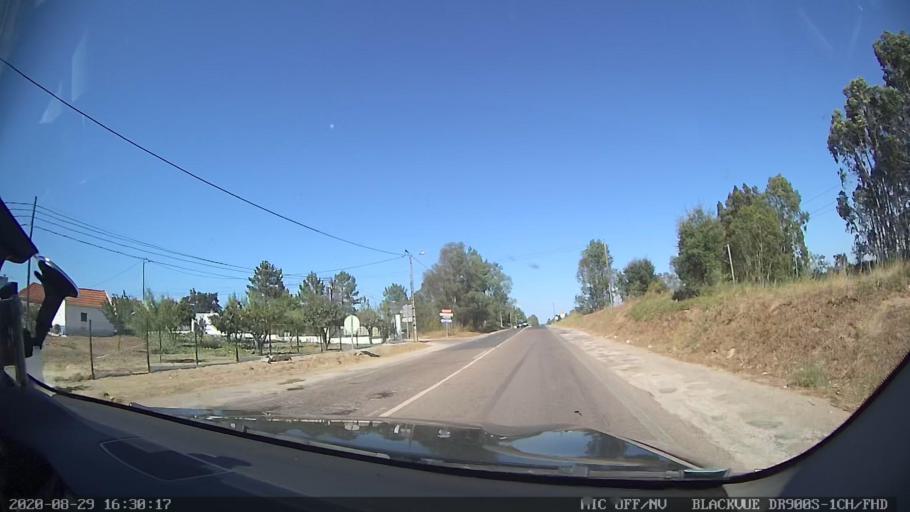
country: PT
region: Setubal
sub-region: Setubal
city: Setubal
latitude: 38.5599
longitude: -8.7893
